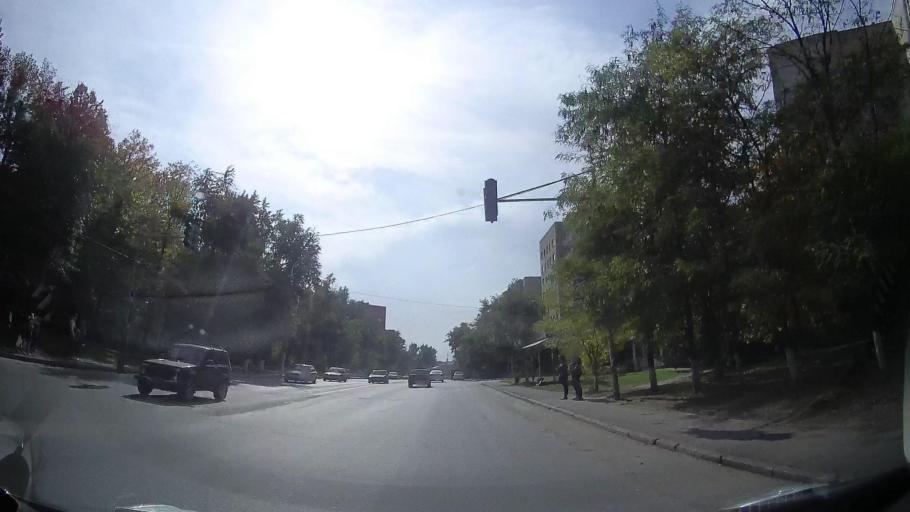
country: RU
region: Rostov
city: Severnyy
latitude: 47.2815
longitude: 39.7077
